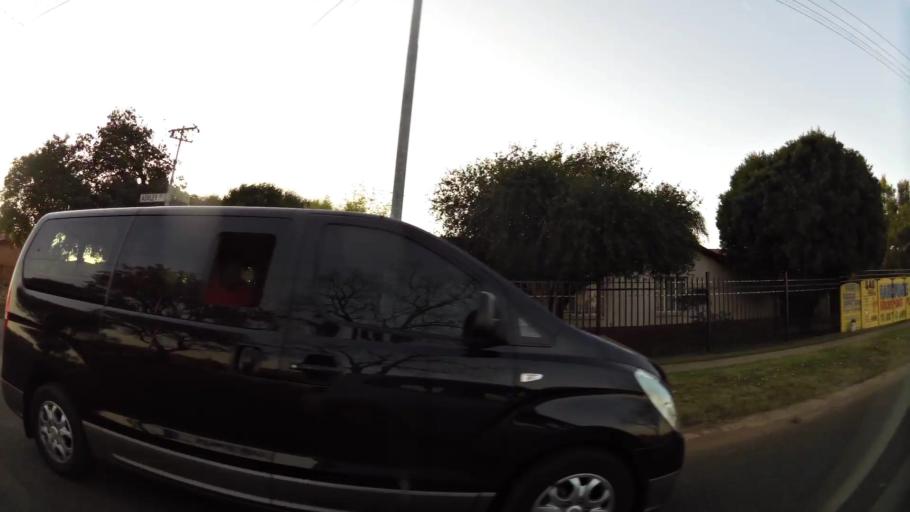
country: ZA
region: Gauteng
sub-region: City of Tshwane Metropolitan Municipality
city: Pretoria
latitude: -25.7445
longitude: 28.1328
